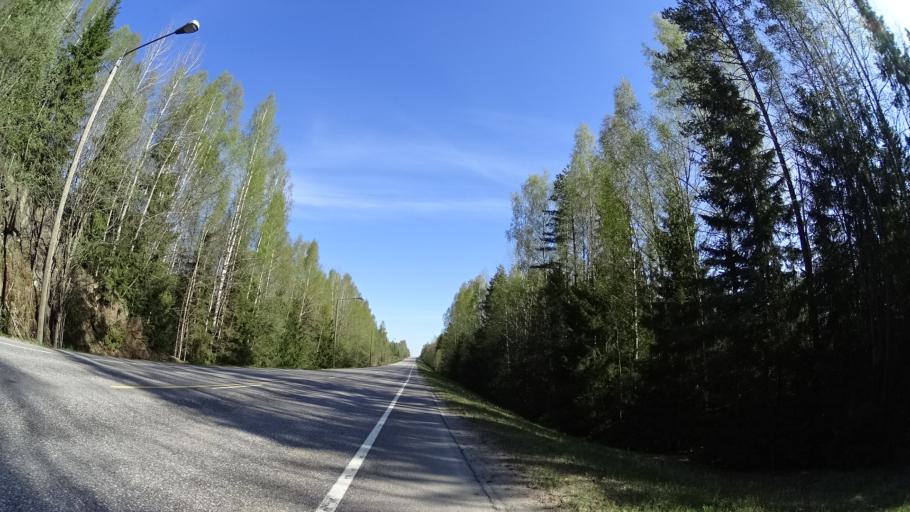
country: FI
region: Uusimaa
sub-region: Helsinki
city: Nurmijaervi
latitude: 60.3763
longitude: 24.8061
